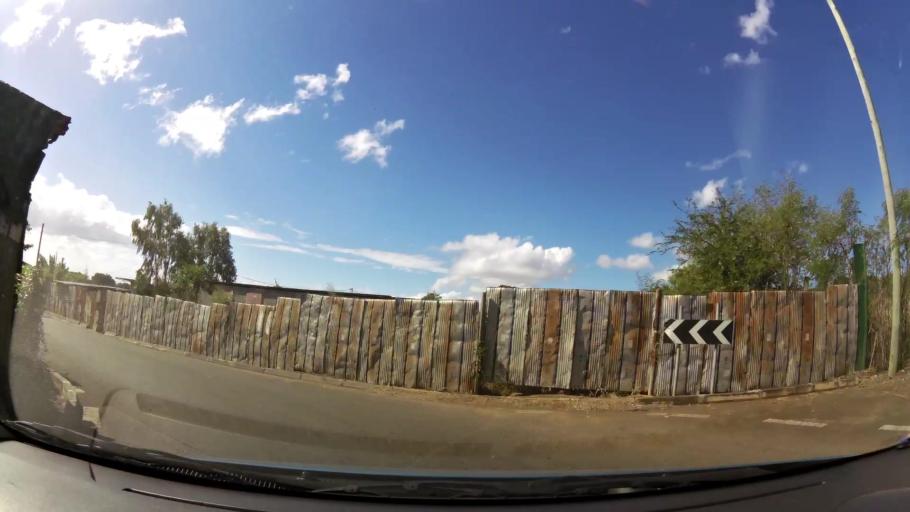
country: MU
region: Black River
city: Gros Cailloux
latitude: -20.2308
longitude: 57.4278
